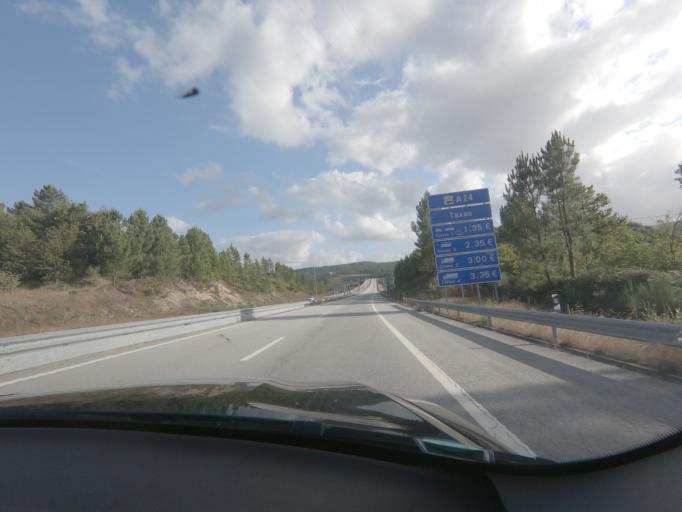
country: PT
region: Viseu
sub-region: Viseu
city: Campo
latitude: 40.7557
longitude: -7.9217
